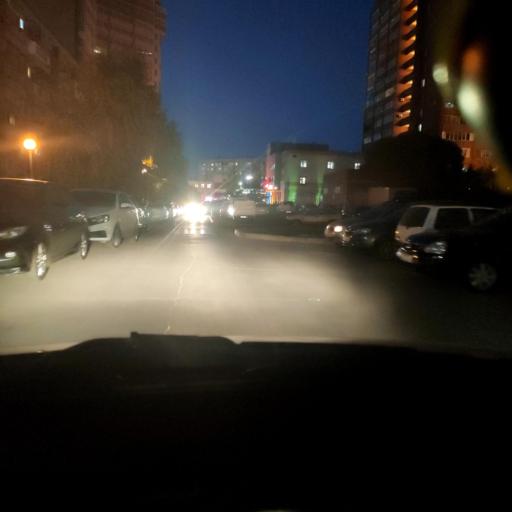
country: RU
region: Samara
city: Tol'yatti
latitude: 53.5396
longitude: 49.3416
